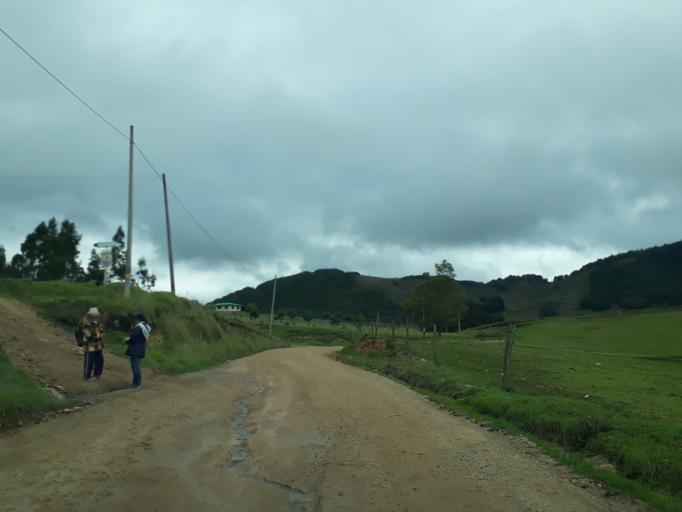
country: CO
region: Cundinamarca
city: Cucunuba
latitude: 5.1998
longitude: -73.7552
